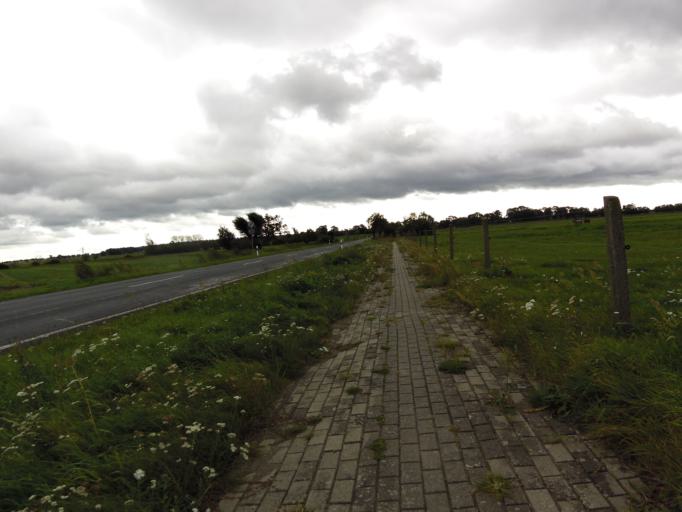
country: DE
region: Saxony-Anhalt
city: Hohenberg-Krusemark
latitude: 52.7119
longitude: 11.9536
